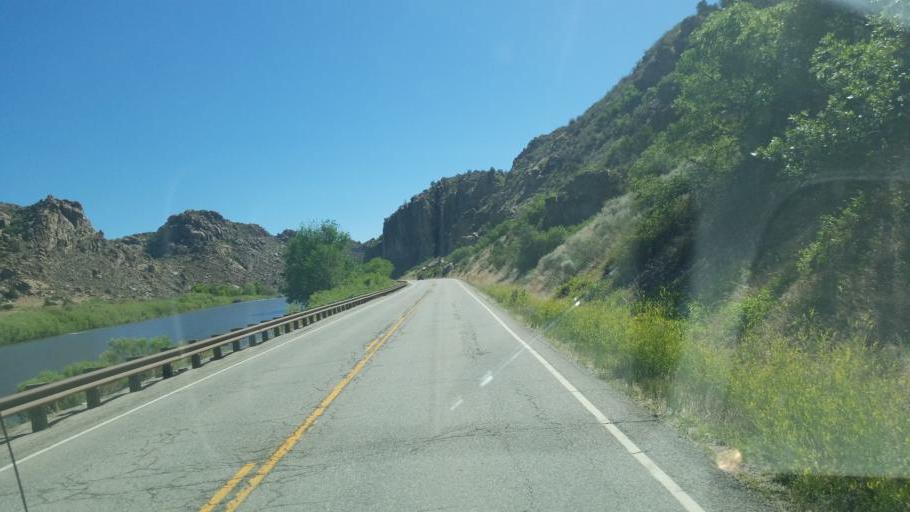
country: US
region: Colorado
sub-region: Custer County
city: Westcliffe
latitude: 38.3915
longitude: -105.6414
